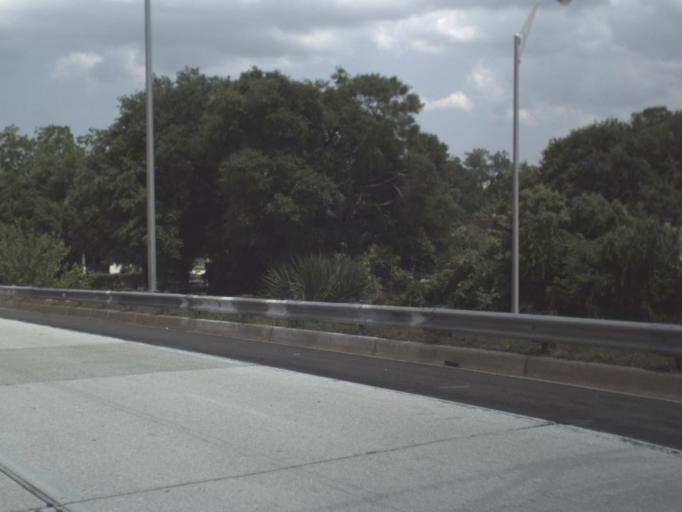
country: US
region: Florida
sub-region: Duval County
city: Jacksonville
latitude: 30.3563
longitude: -81.6532
